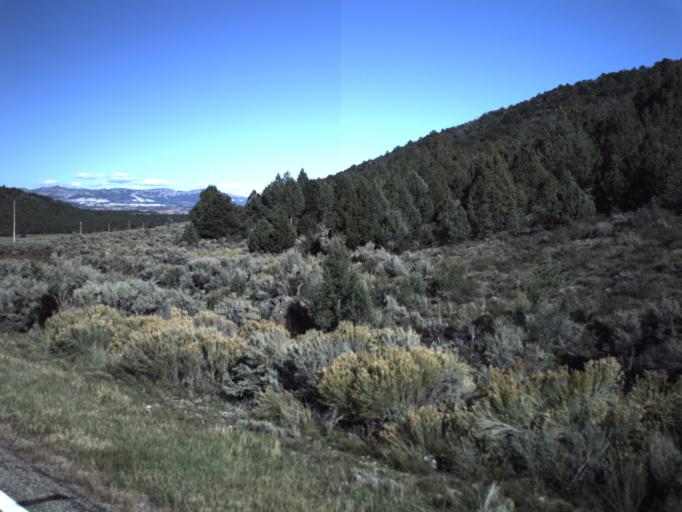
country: US
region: Utah
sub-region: Garfield County
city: Panguitch
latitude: 37.7626
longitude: -112.5031
